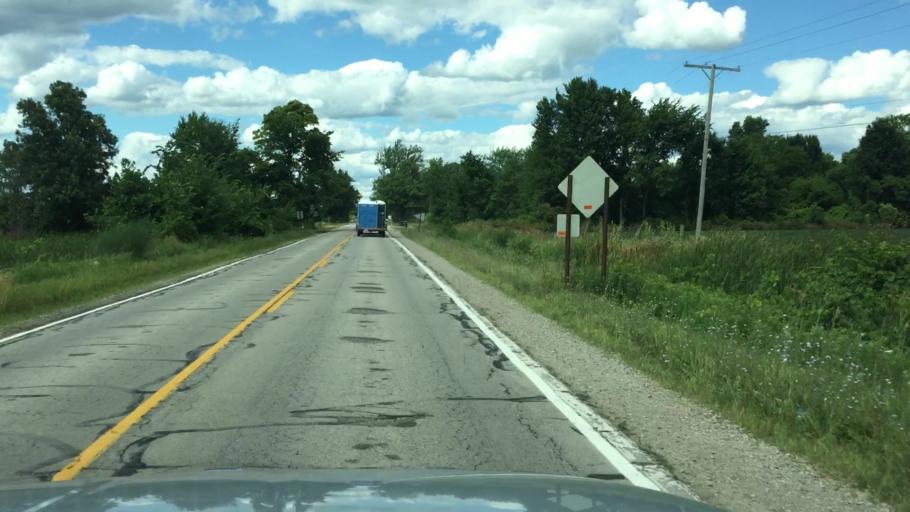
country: US
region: Michigan
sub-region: Saint Clair County
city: Capac
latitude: 42.9483
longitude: -82.9433
